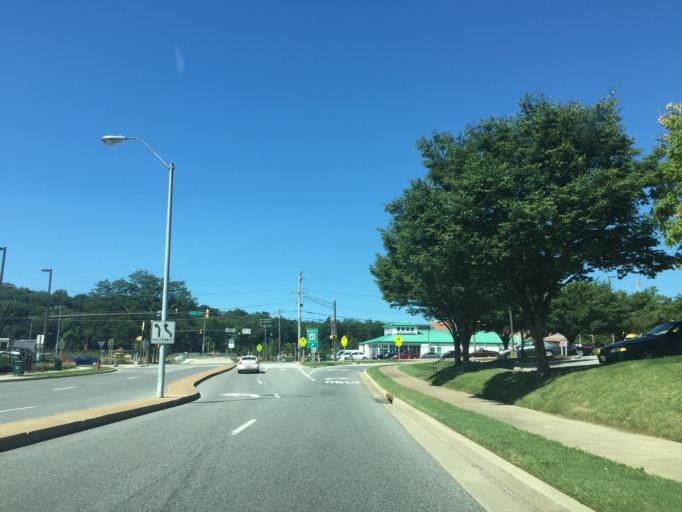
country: US
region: Maryland
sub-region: Baltimore County
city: Towson
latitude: 39.4102
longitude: -76.6079
